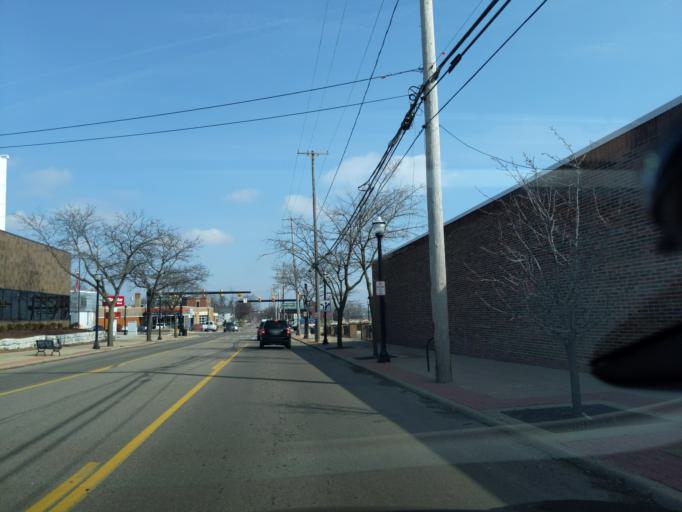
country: US
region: Michigan
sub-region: Jackson County
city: Jackson
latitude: 42.2467
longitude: -84.4117
